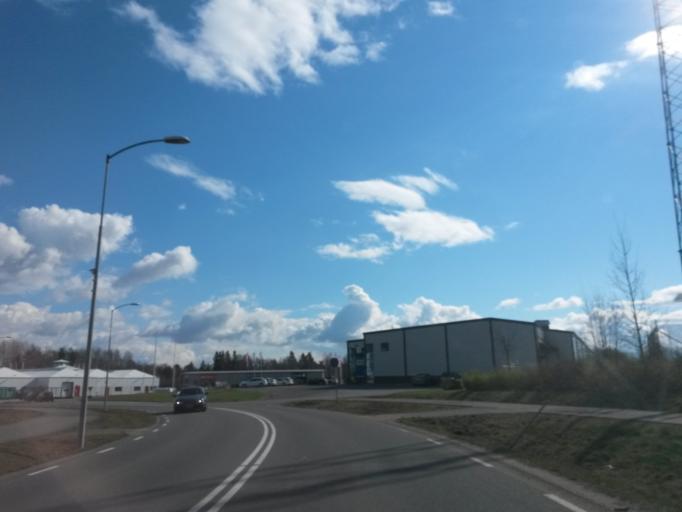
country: SE
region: Vaestra Goetaland
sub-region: Skovde Kommun
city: Skoevde
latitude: 58.4087
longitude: 13.8736
